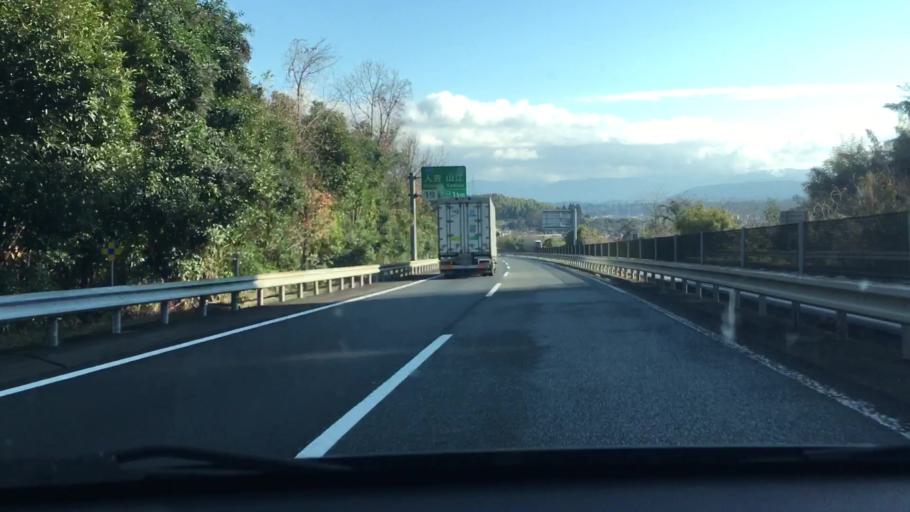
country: JP
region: Kumamoto
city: Hitoyoshi
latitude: 32.2394
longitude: 130.7609
